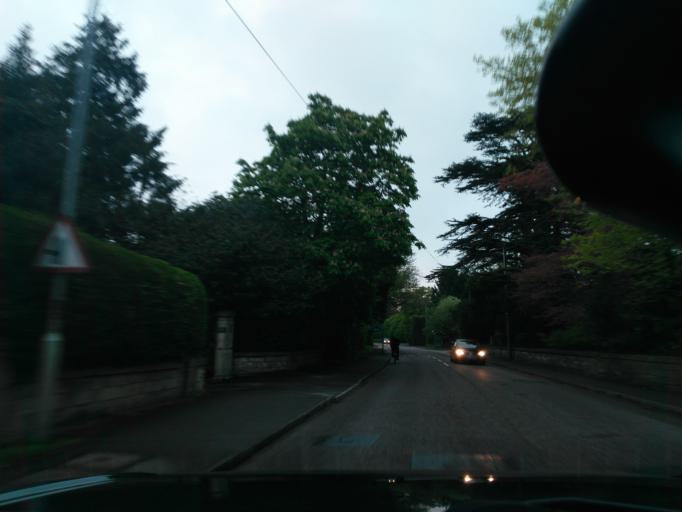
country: GB
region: England
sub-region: Wiltshire
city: Trowbridge
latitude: 51.3251
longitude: -2.1935
